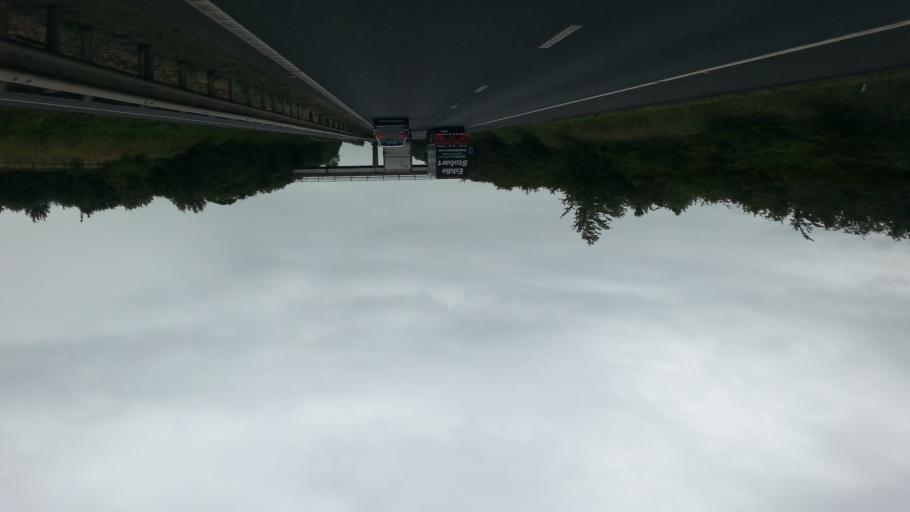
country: GB
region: England
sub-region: Cambridgeshire
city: Duxford
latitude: 52.0891
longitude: 0.1471
